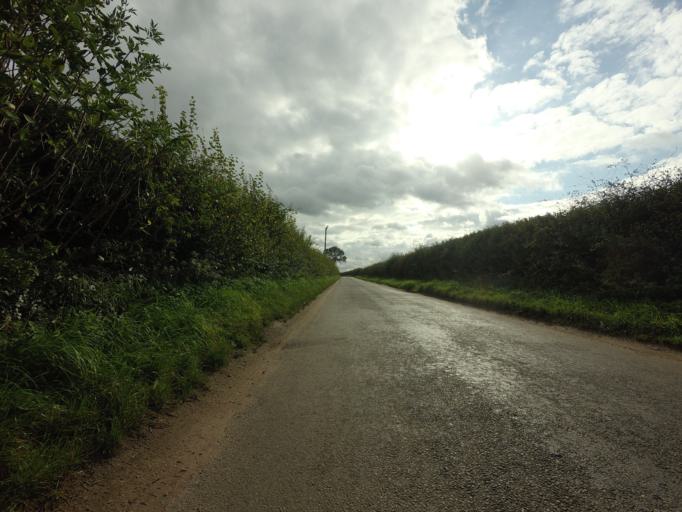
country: GB
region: England
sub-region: Norfolk
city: Snettisham
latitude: 52.8759
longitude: 0.5144
